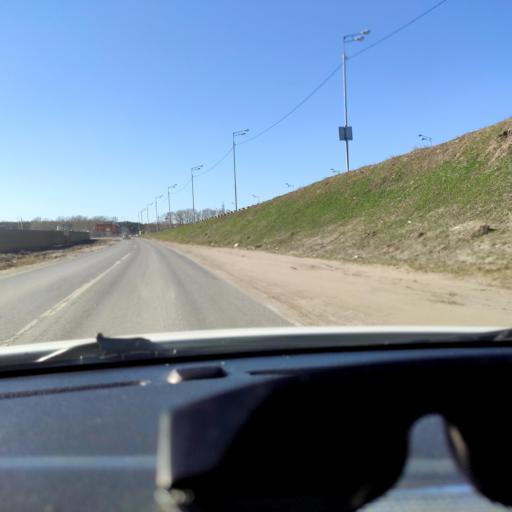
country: RU
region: Tatarstan
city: Vysokaya Gora
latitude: 55.8855
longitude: 49.2343
